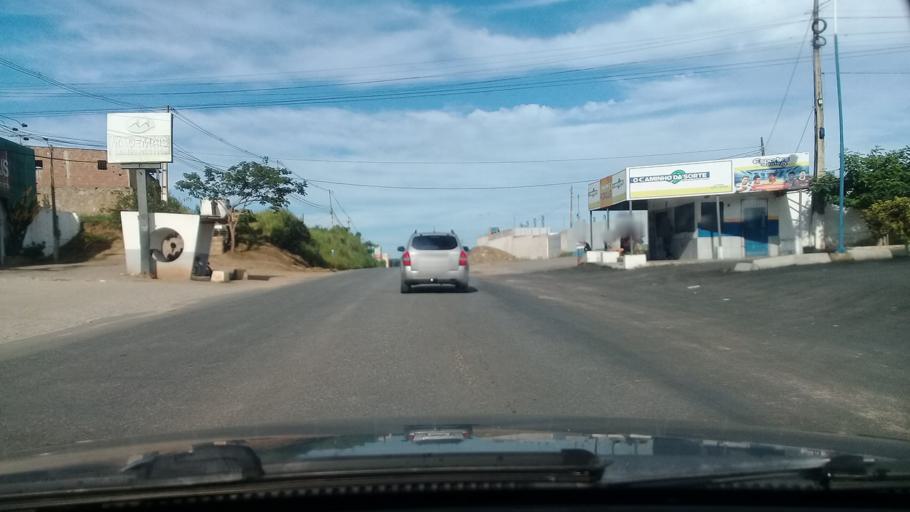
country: BR
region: Pernambuco
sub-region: Vitoria De Santo Antao
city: Vitoria de Santo Antao
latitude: -8.1146
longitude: -35.2787
